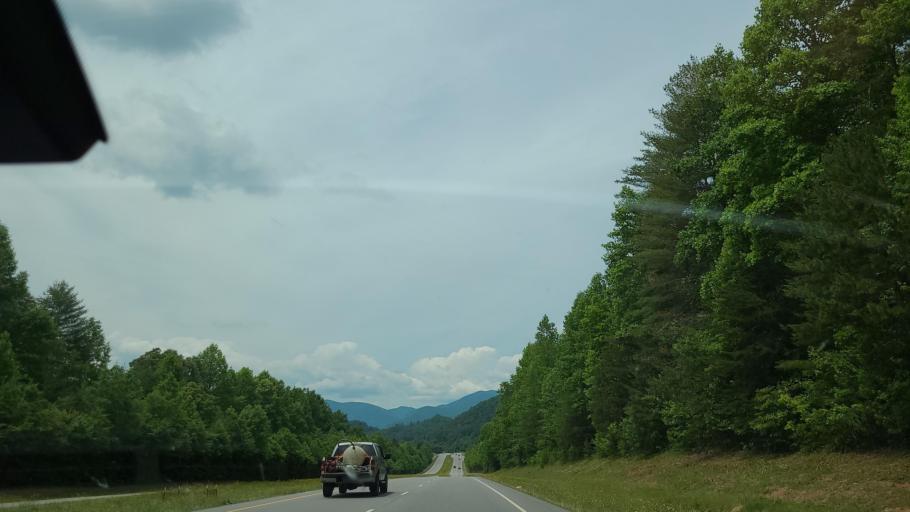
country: US
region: North Carolina
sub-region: Macon County
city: Franklin
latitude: 35.1615
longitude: -83.4461
